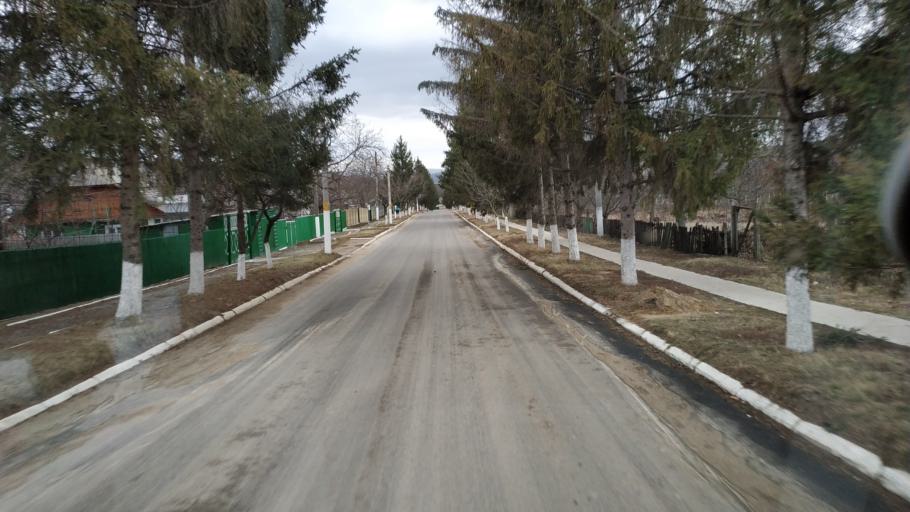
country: MD
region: Calarasi
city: Calarasi
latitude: 47.2058
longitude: 28.2437
